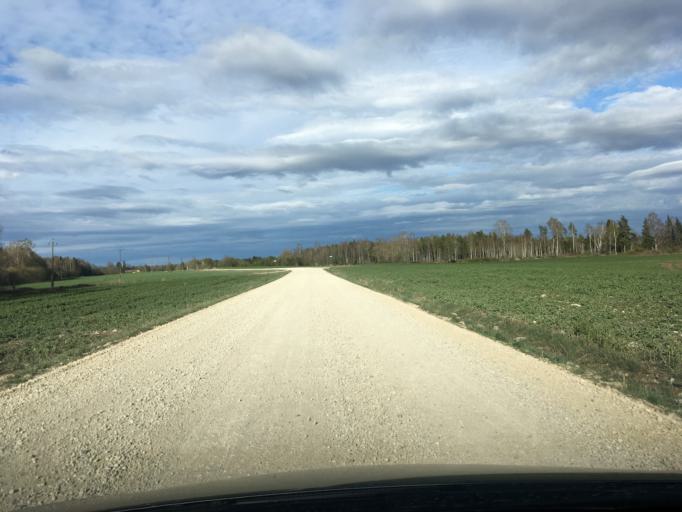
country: EE
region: Raplamaa
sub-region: Maerjamaa vald
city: Marjamaa
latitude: 58.9714
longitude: 24.3401
